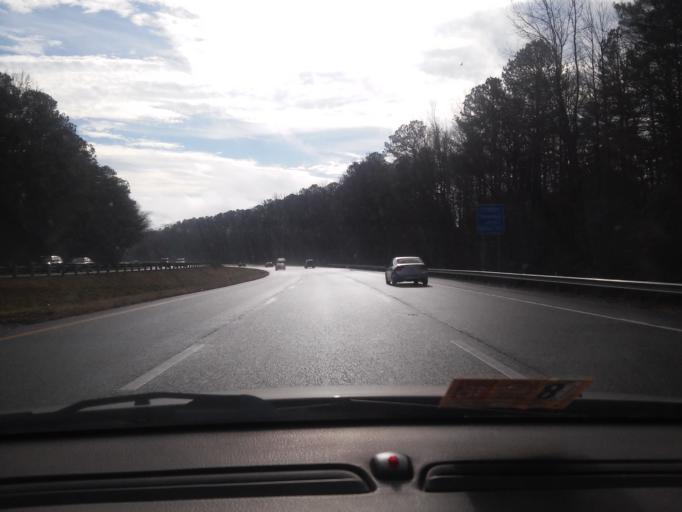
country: US
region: Virginia
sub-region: Henrico County
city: Dumbarton
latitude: 37.6011
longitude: -77.5001
